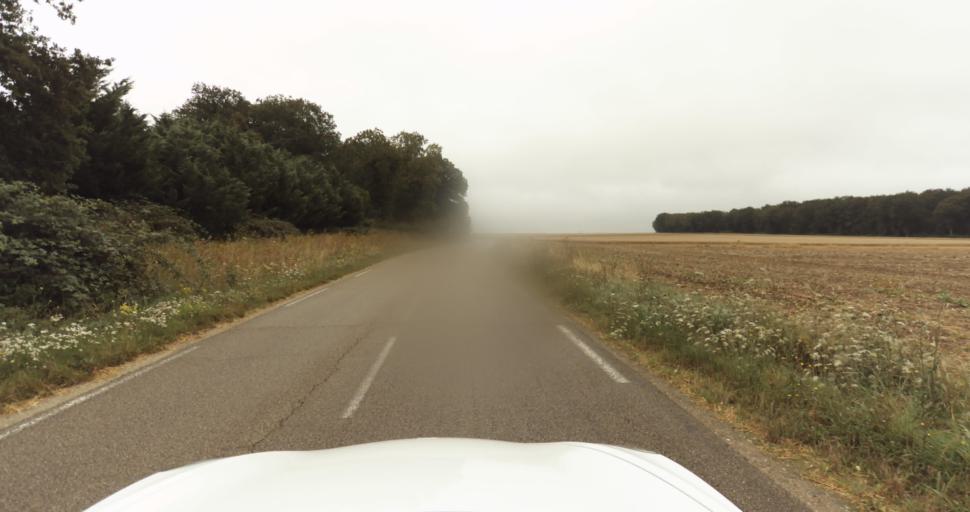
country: FR
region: Haute-Normandie
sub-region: Departement de l'Eure
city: Normanville
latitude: 49.0924
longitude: 1.1703
